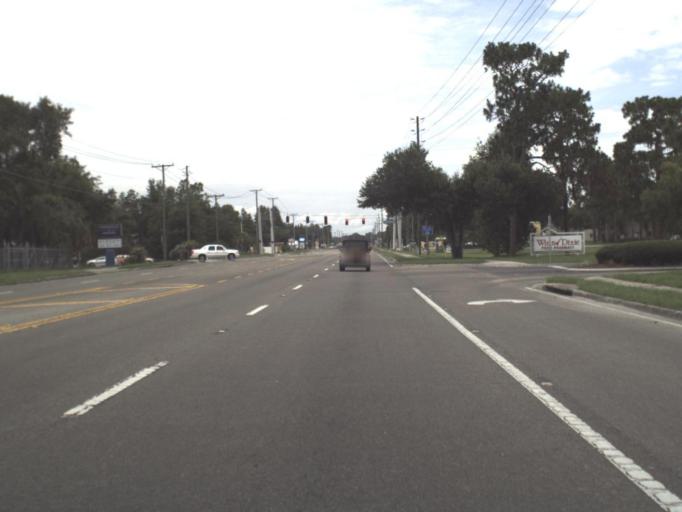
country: US
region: Florida
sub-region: Citrus County
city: Crystal River
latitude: 28.8812
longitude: -82.5405
